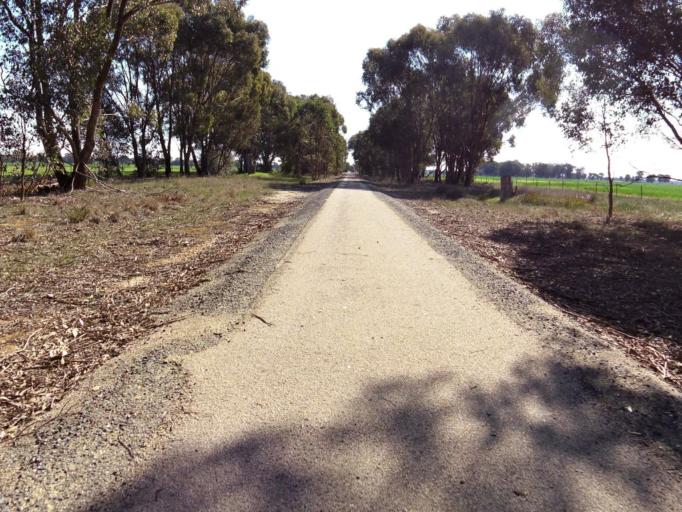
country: AU
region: New South Wales
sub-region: Corowa Shire
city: Corowa
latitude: -36.0232
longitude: 146.4273
